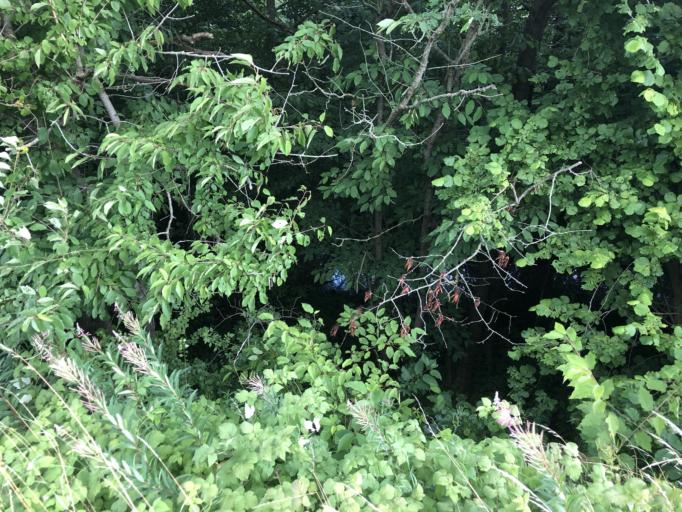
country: DK
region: South Denmark
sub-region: Vejle Kommune
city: Borkop
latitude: 55.6544
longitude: 9.6494
